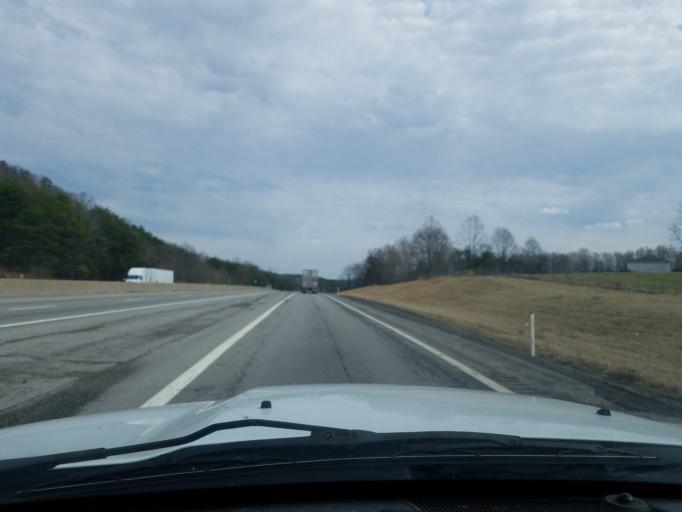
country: US
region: West Virginia
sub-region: Putnam County
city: Teays Valley
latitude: 38.4551
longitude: -81.8921
